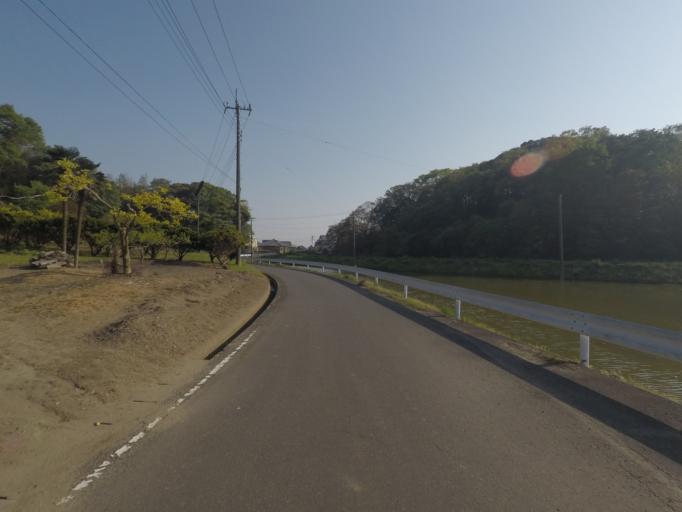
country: JP
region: Ibaraki
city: Inashiki
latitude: 36.0671
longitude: 140.3586
